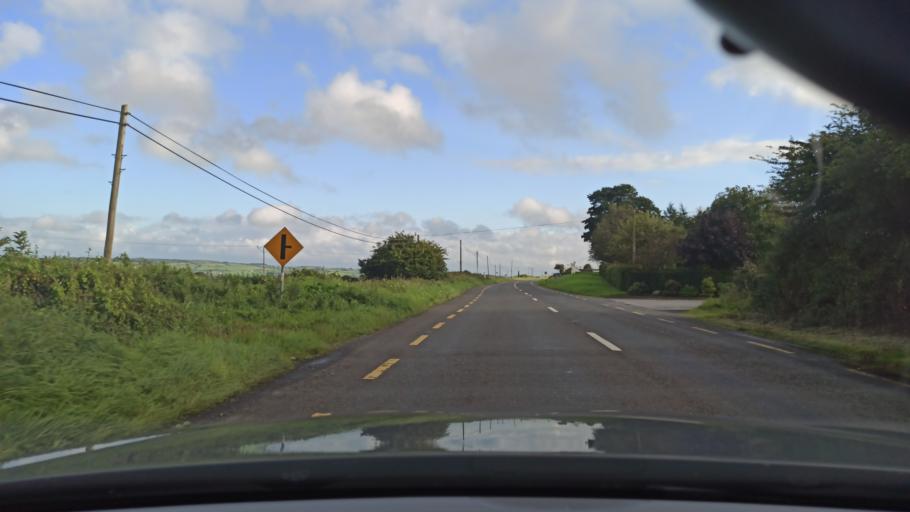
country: IE
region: Munster
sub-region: North Tipperary
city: Roscrea
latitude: 52.9355
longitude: -7.7877
